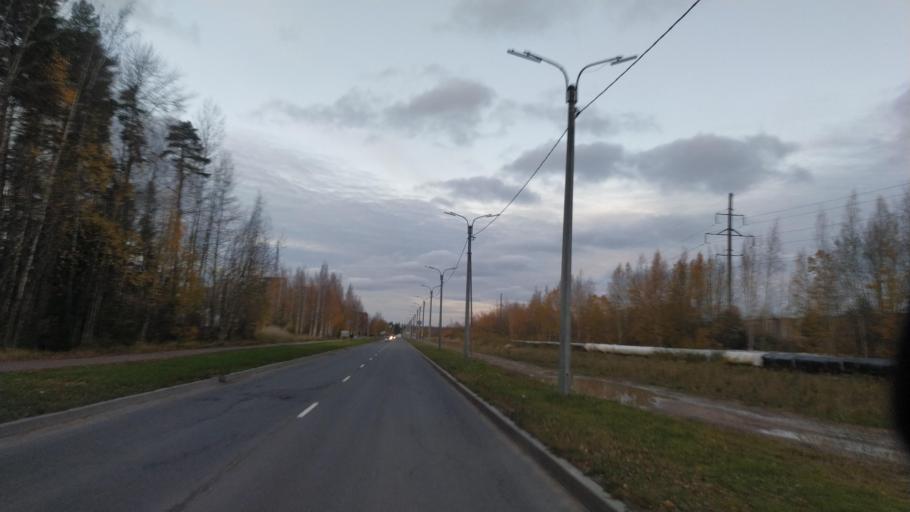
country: RU
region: Leningrad
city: Sosnovyy Bor
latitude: 59.9093
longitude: 29.1008
